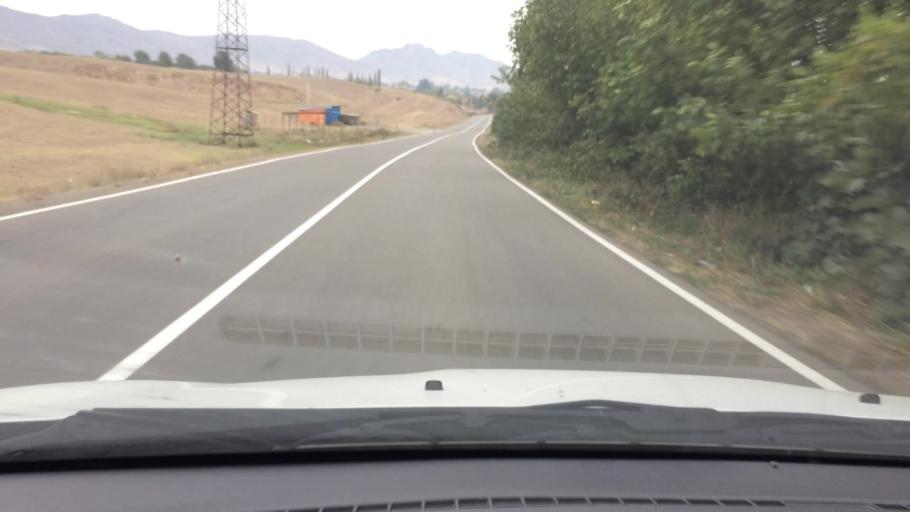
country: AM
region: Tavush
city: Bagratashen
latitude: 41.2863
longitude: 44.7898
